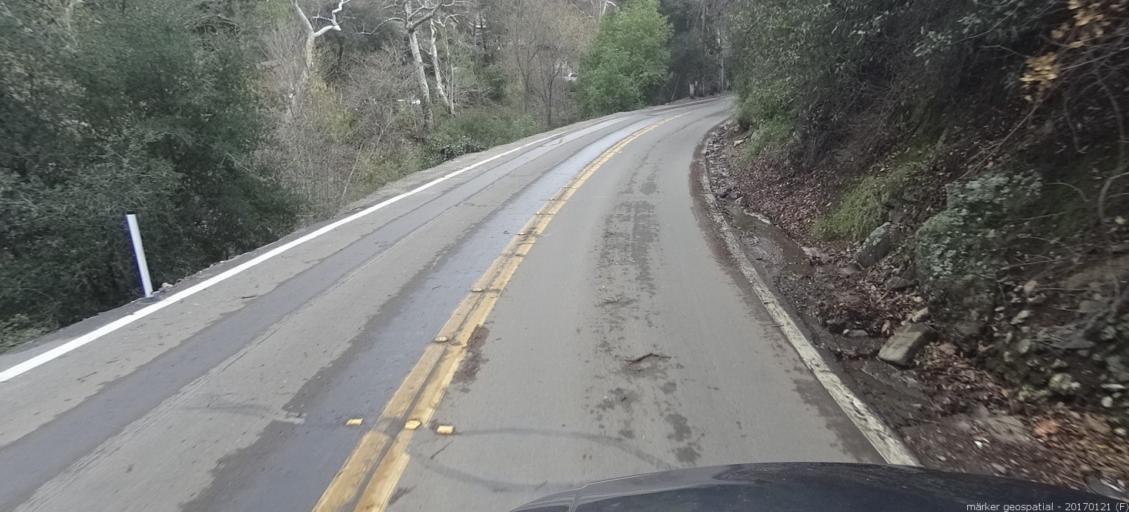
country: US
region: California
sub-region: Orange County
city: Portola Hills
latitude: 33.7461
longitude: -117.6076
